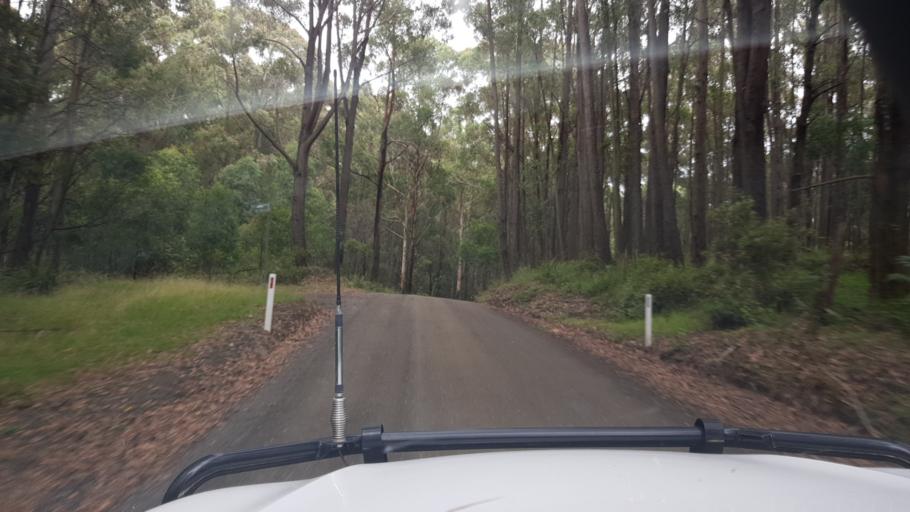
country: AU
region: Victoria
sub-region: Baw Baw
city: Warragul
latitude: -38.0096
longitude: 145.8867
